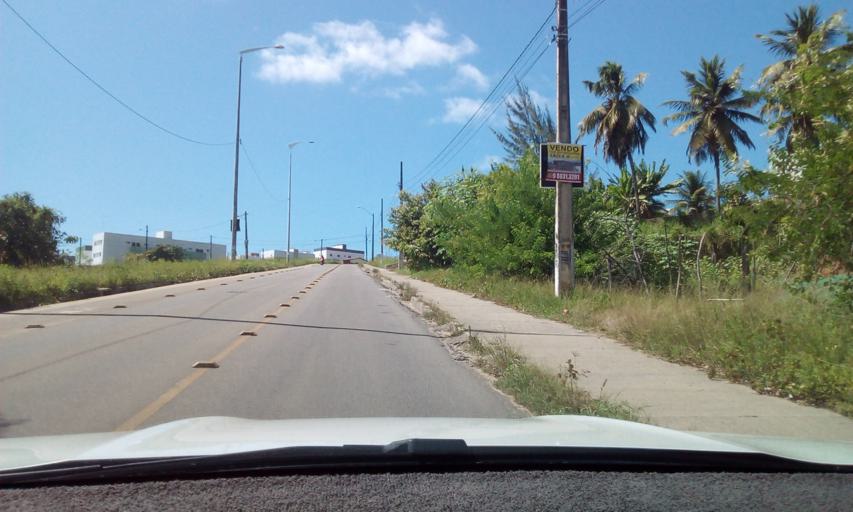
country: BR
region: Paraiba
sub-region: Joao Pessoa
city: Joao Pessoa
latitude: -7.1955
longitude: -34.8363
